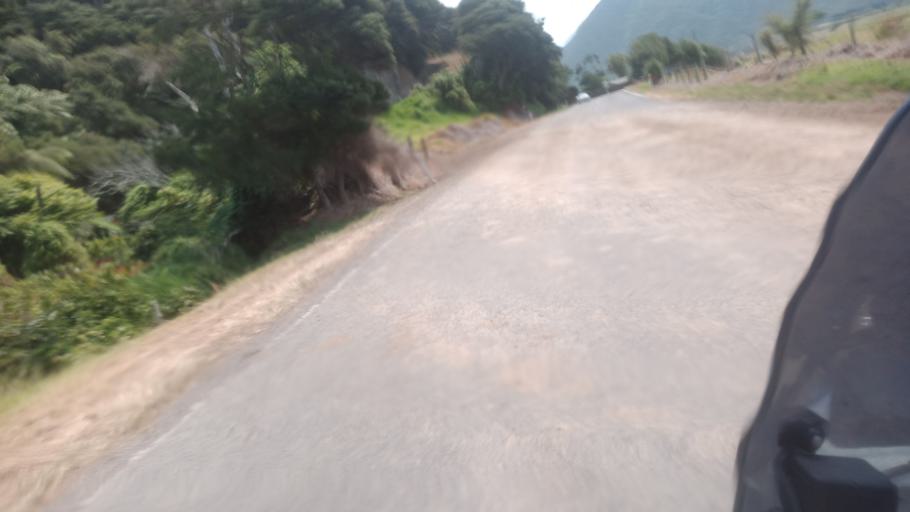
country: NZ
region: Bay of Plenty
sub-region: Opotiki District
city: Opotiki
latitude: -37.5739
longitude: 178.0160
